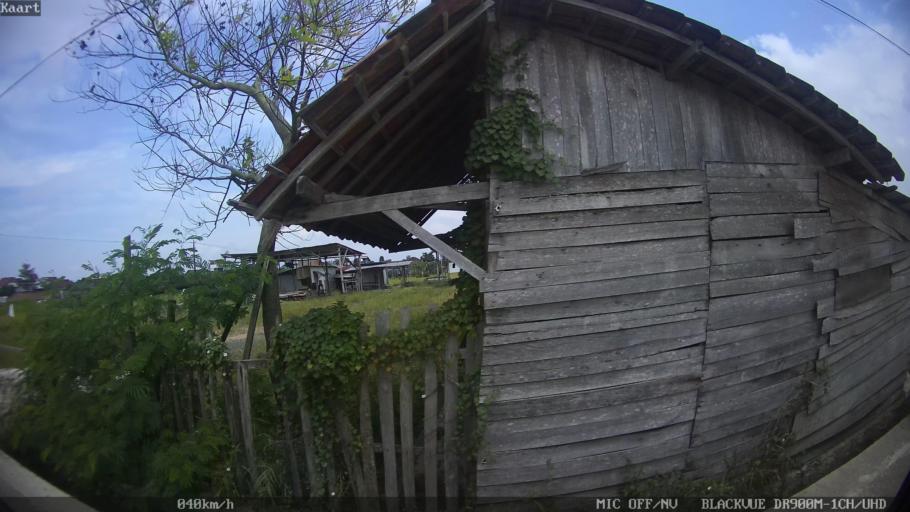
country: ID
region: Lampung
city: Kedaton
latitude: -5.3696
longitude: 105.3084
